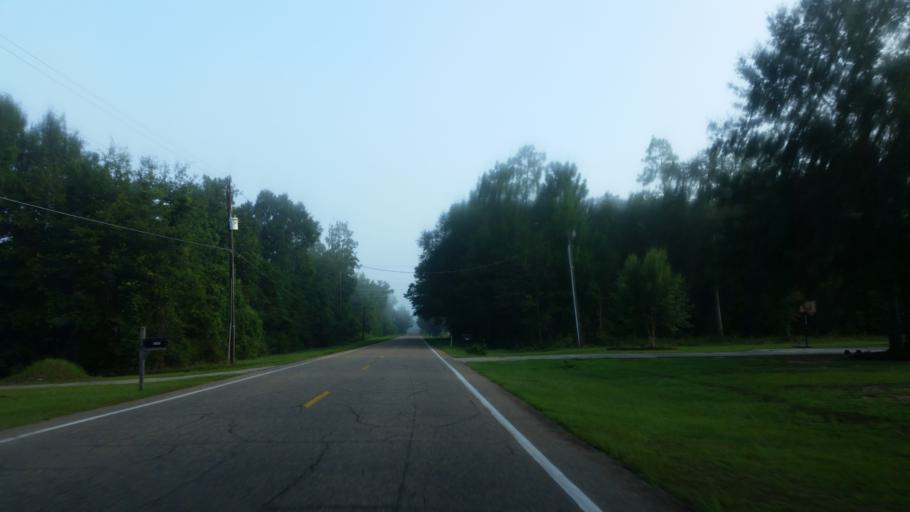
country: US
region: Florida
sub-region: Escambia County
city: Molino
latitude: 30.7350
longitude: -87.3464
